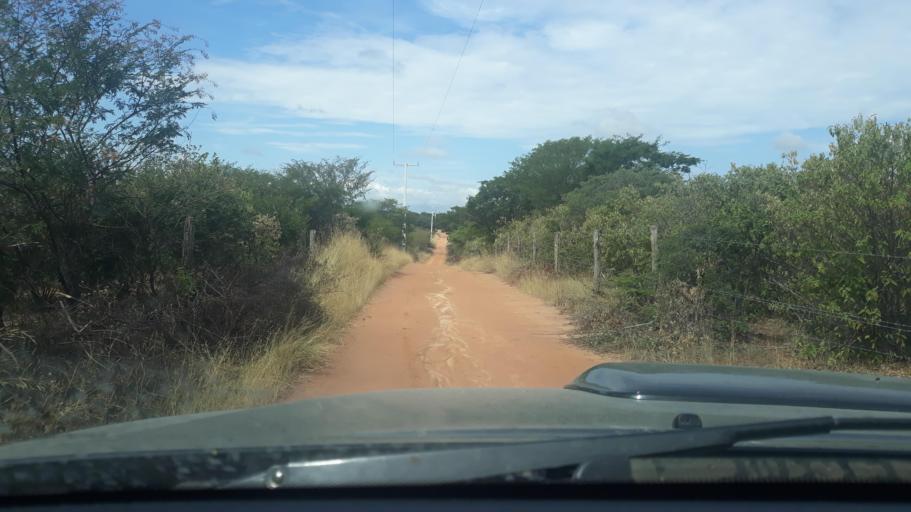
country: BR
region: Bahia
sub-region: Riacho De Santana
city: Riacho de Santana
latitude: -13.8516
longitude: -43.0533
